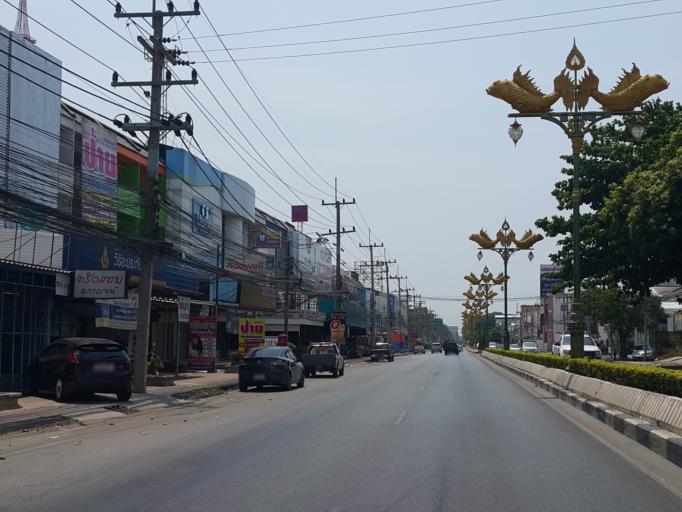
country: TH
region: Kanchanaburi
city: Kanchanaburi
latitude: 14.0361
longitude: 99.5213
